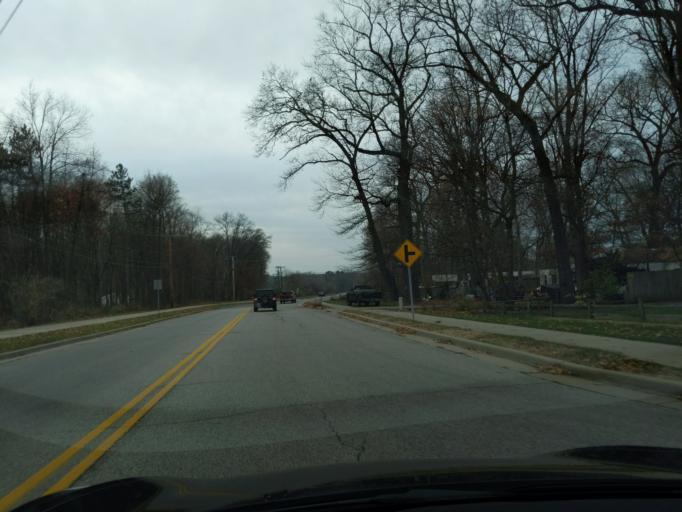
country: US
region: Indiana
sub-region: Saint Joseph County
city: Georgetown
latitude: 41.7304
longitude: -86.2636
